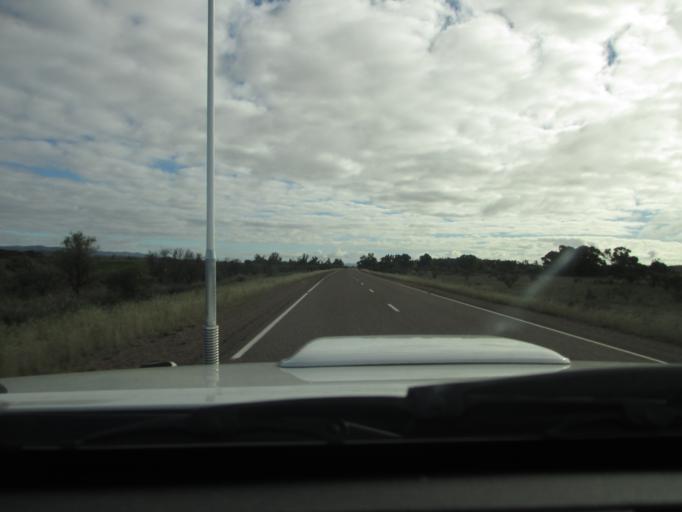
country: AU
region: South Australia
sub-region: Flinders Ranges
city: Quorn
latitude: -32.4833
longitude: 138.5438
